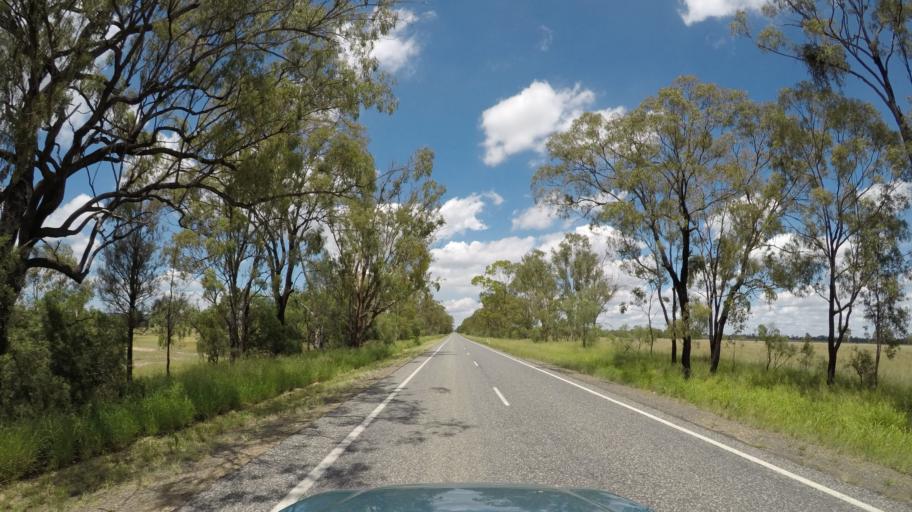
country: AU
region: Queensland
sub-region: Toowoomba
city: Oakey
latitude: -27.8884
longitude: 151.2178
